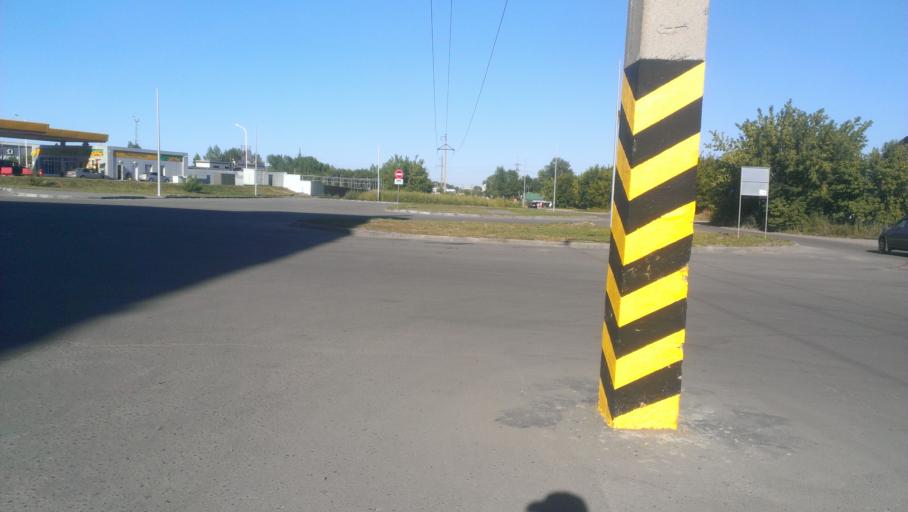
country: RU
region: Altai Krai
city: Novosilikatnyy
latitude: 53.3259
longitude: 83.6923
